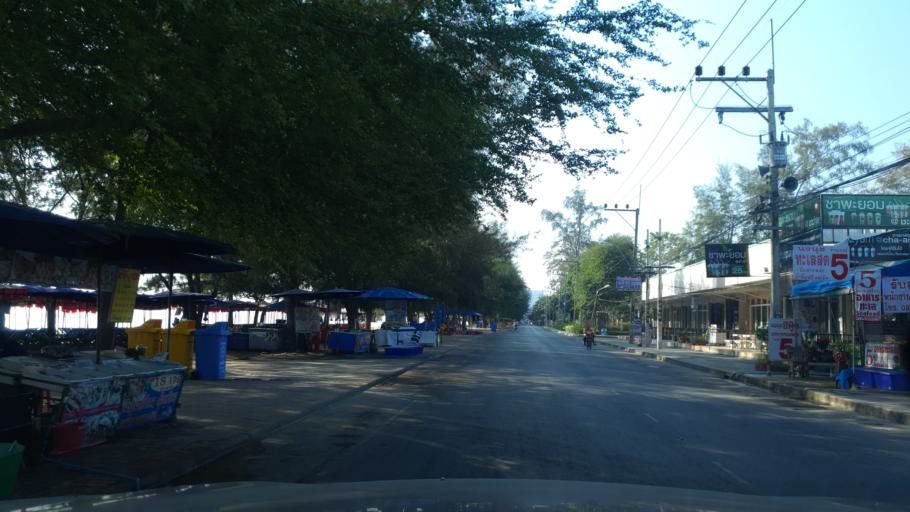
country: TH
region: Phetchaburi
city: Cha-am
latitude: 12.7804
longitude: 99.9785
